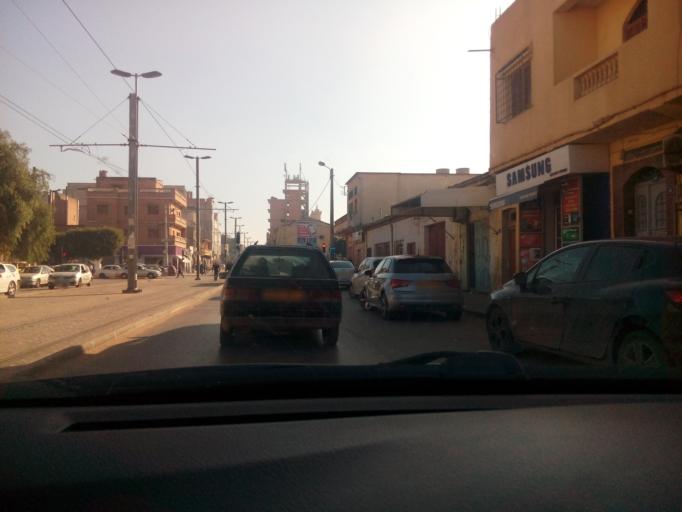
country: DZ
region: Oran
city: Es Senia
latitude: 35.6514
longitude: -0.6261
